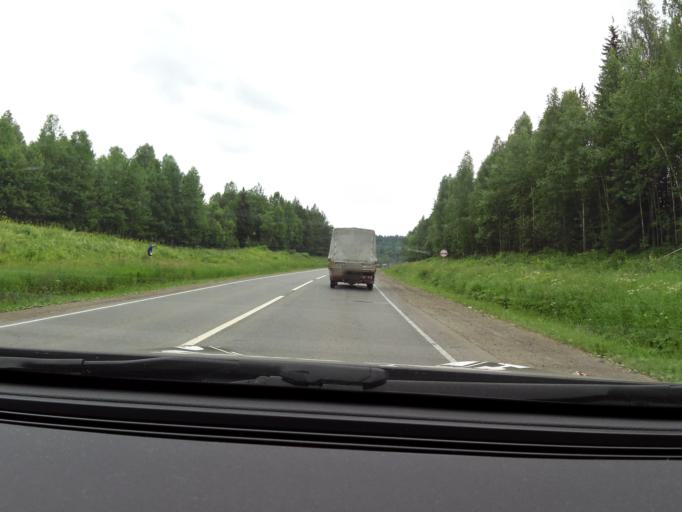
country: RU
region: Perm
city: Kukushtan
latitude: 57.5942
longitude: 56.5400
